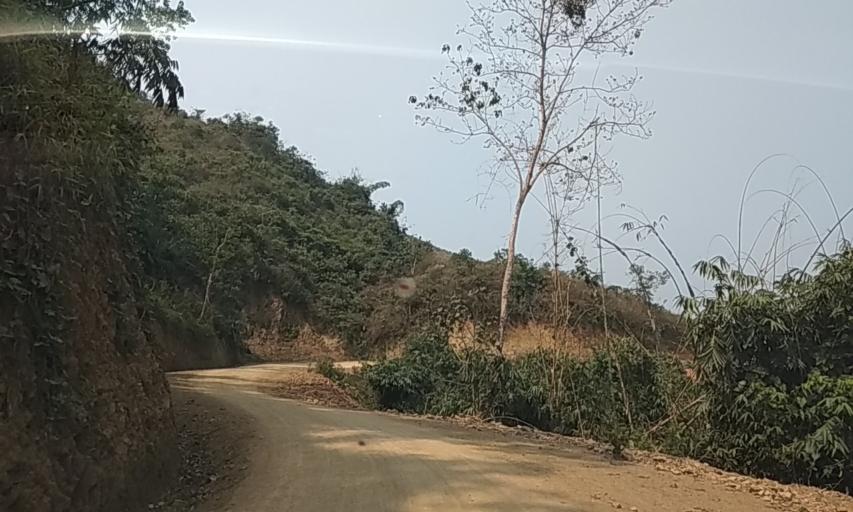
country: LA
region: Phongsali
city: Phongsali
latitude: 21.4761
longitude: 102.4395
